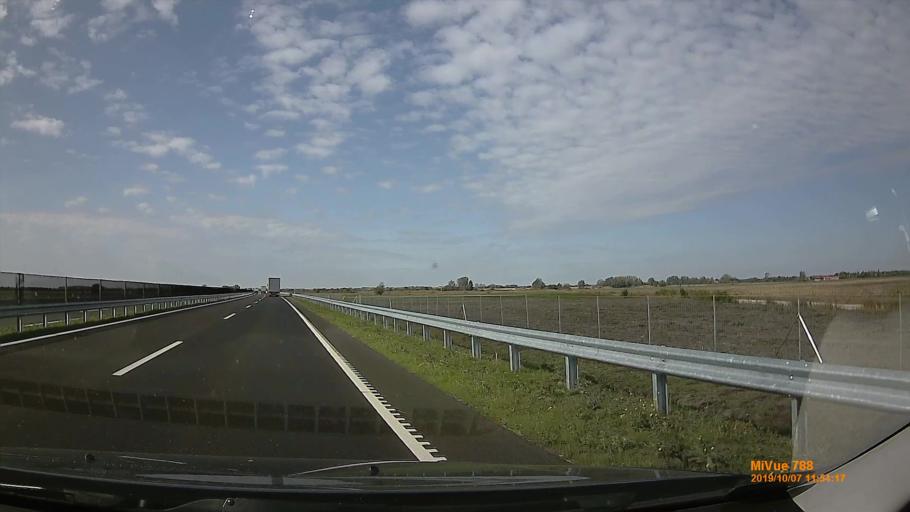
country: HU
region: Bekes
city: Szarvas
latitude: 46.8198
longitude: 20.5940
